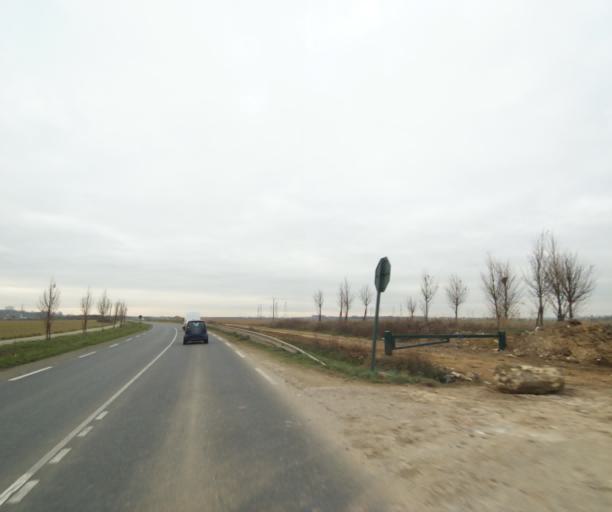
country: FR
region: Ile-de-France
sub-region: Departement du Val-d'Oise
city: Villiers-le-Bel
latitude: 49.0090
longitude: 2.4235
